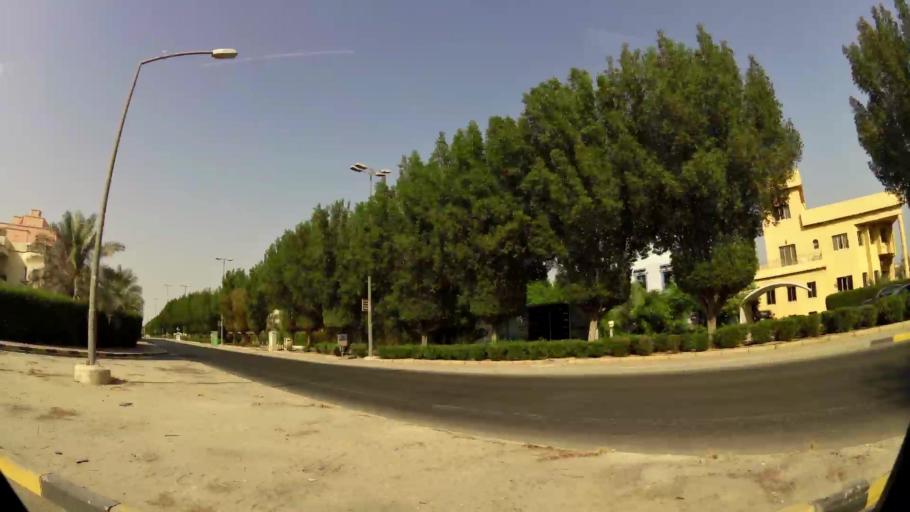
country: KW
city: Bayan
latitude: 29.2812
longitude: 48.0462
